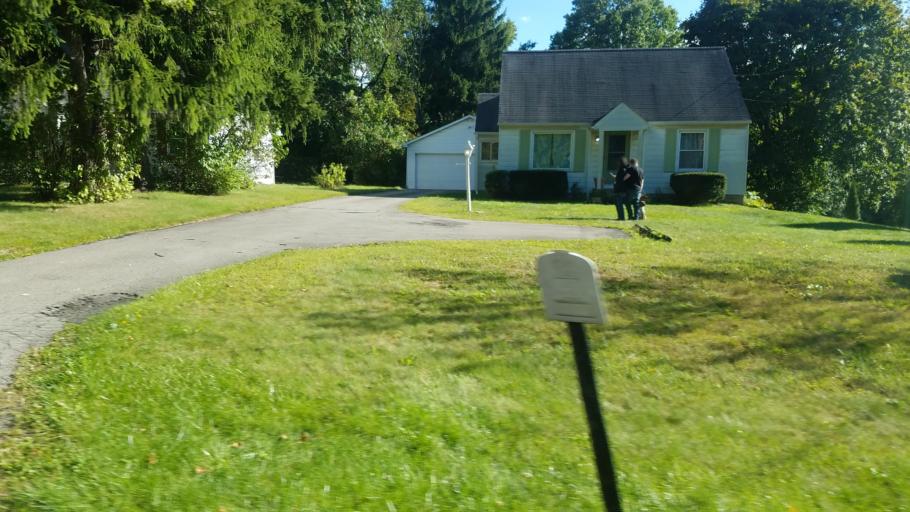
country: US
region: Ohio
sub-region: Mahoning County
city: Canfield
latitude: 41.0460
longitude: -80.7154
